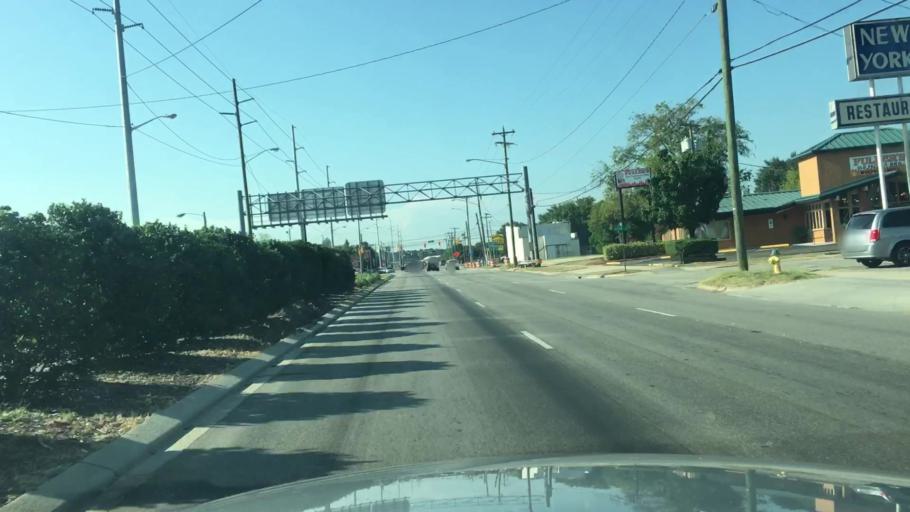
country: US
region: North Carolina
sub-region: Cumberland County
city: Fayetteville
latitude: 35.0498
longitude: -78.8649
